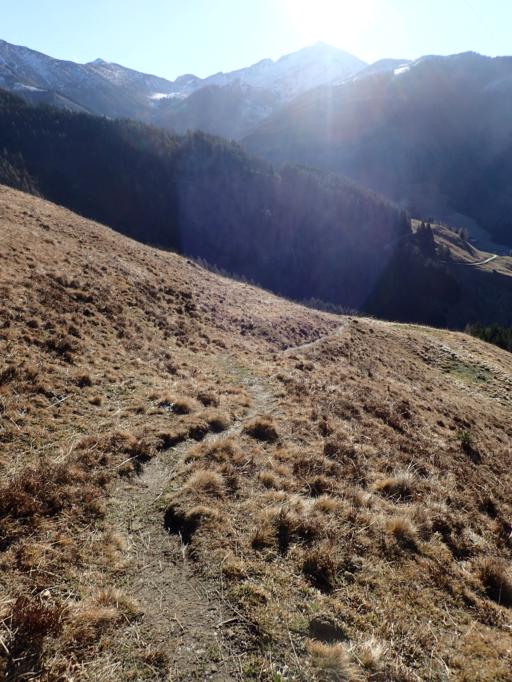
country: AT
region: Salzburg
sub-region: Politischer Bezirk Zell am See
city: Rauris
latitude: 47.2412
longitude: 13.0063
